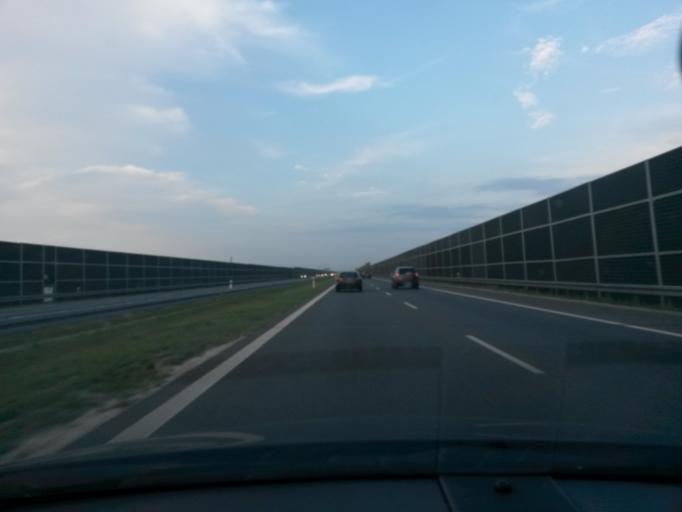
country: PL
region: Masovian Voivodeship
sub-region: Powiat grodziski
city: Milanowek
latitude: 52.1512
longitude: 20.6600
